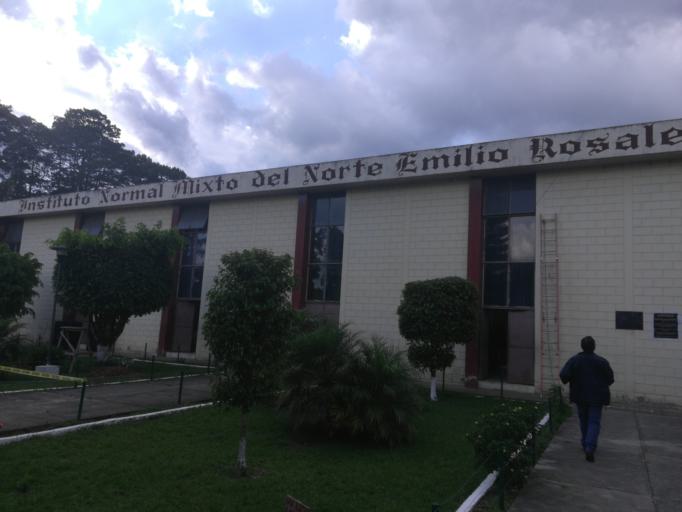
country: GT
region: Alta Verapaz
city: Coban
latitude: 15.4770
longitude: -90.3698
